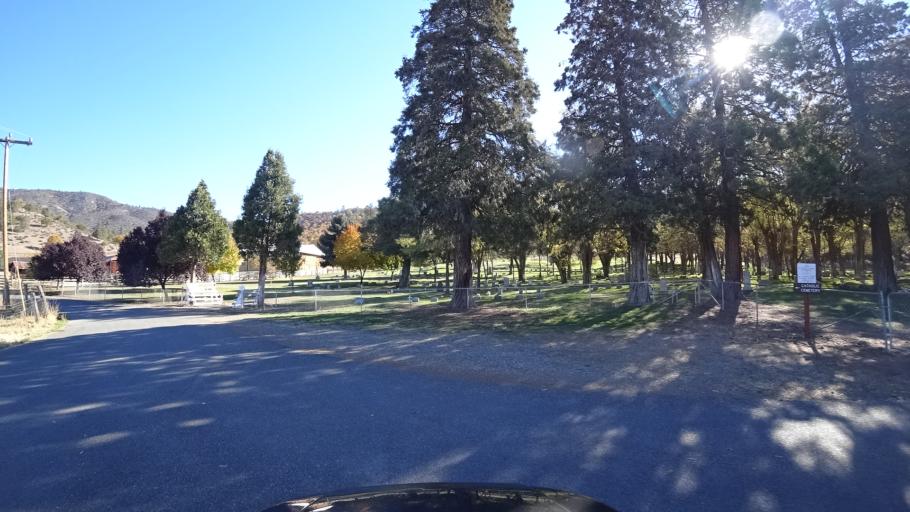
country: US
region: California
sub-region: Siskiyou County
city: Yreka
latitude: 41.5908
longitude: -122.8339
